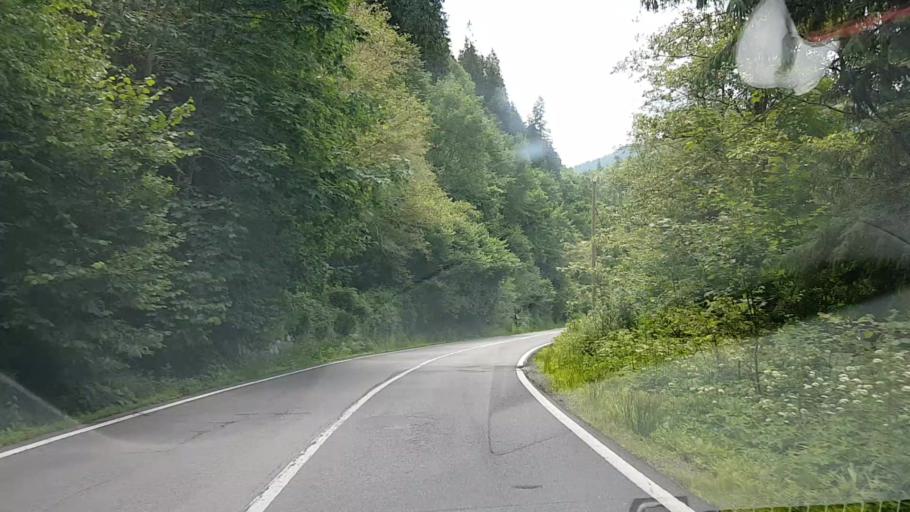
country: RO
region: Suceava
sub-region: Comuna Crucea
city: Crucea
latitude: 47.3782
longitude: 25.5878
